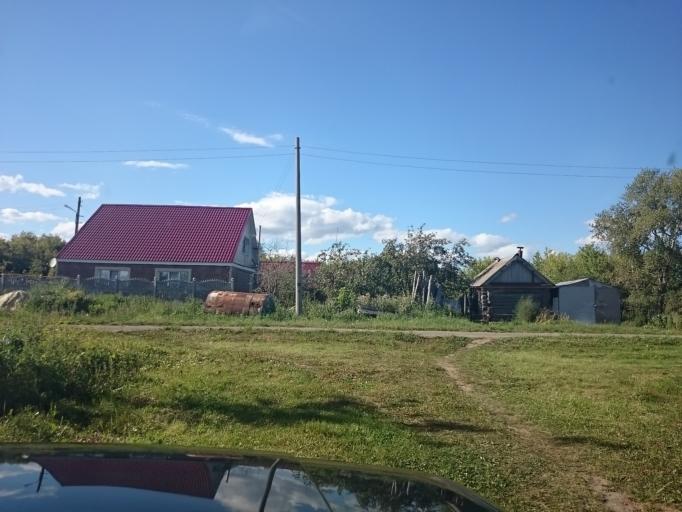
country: RU
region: Mordoviya
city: Kadoshkino
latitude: 54.0219
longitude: 44.4269
